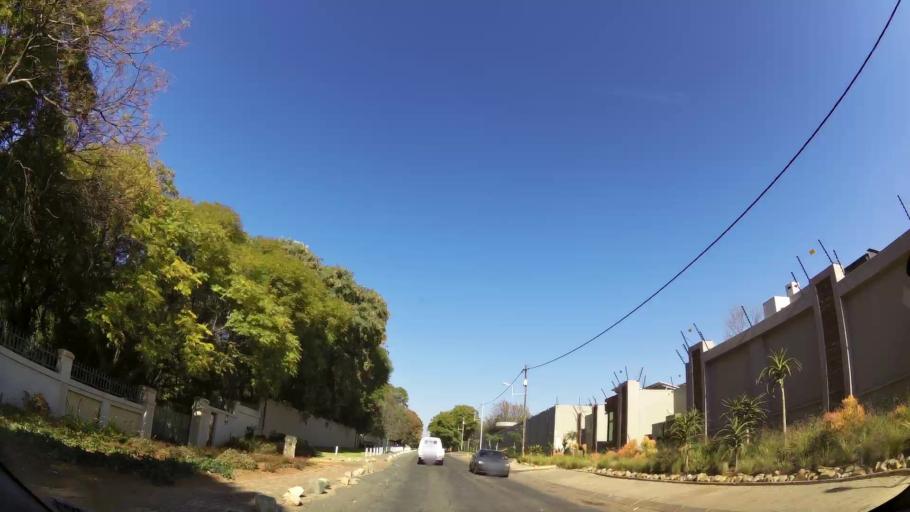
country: ZA
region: Gauteng
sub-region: City of Johannesburg Metropolitan Municipality
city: Midrand
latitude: -26.0599
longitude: 28.0296
